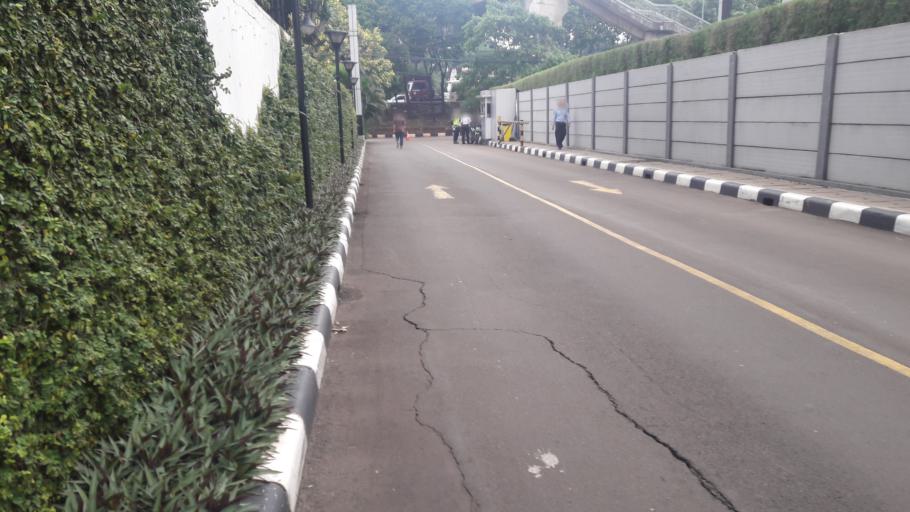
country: ID
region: Jakarta Raya
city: Jakarta
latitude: -6.2916
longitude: 106.8089
